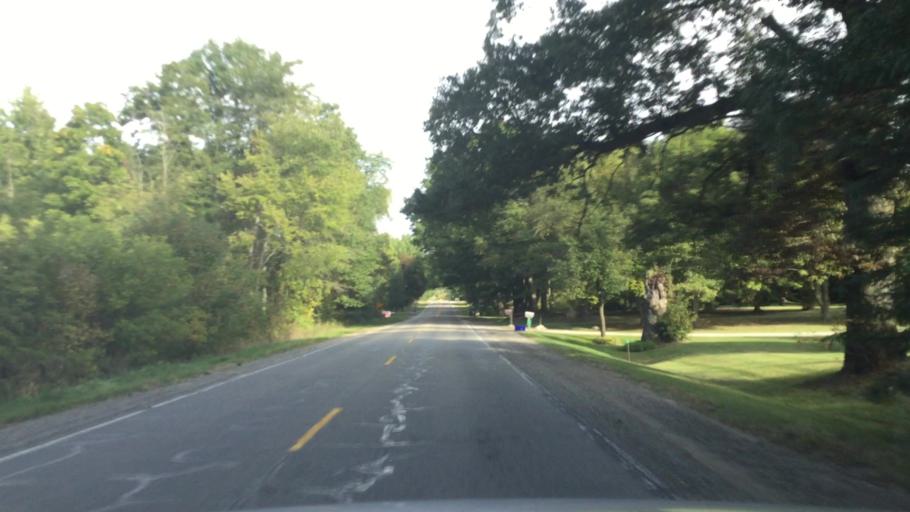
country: US
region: Michigan
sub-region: Livingston County
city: Howell
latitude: 42.5488
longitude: -83.8806
